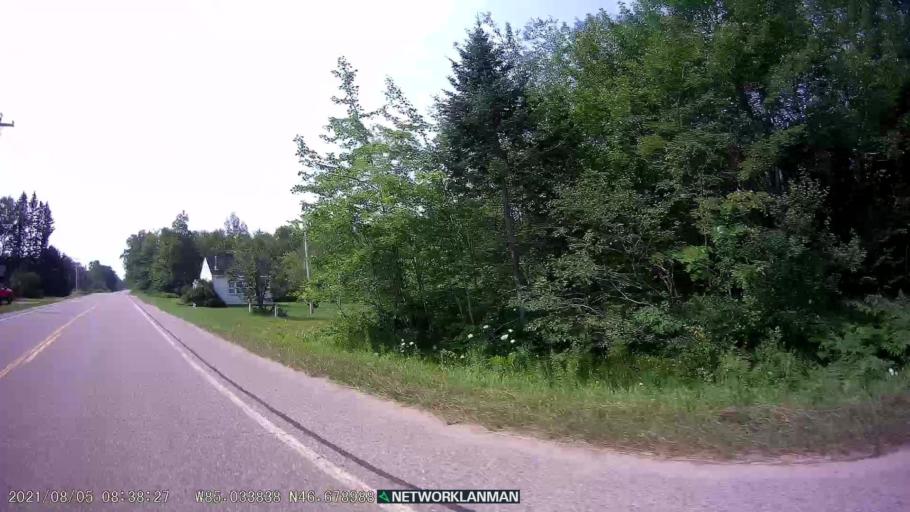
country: US
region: Michigan
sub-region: Luce County
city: Newberry
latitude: 46.6786
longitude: -85.0337
